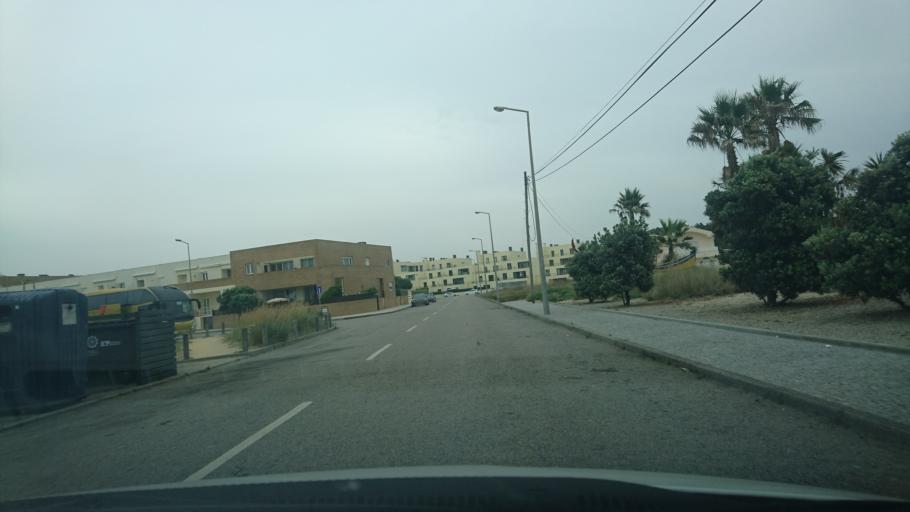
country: PT
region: Aveiro
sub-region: Ovar
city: Esmoriz
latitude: 40.9589
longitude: -8.6524
